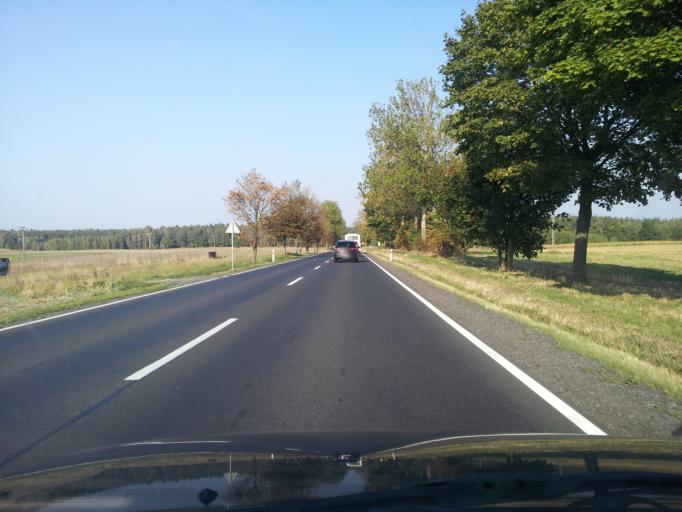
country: PL
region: Kujawsko-Pomorskie
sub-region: Powiat torunski
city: Lubicz Gorny
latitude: 53.1059
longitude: 18.7967
